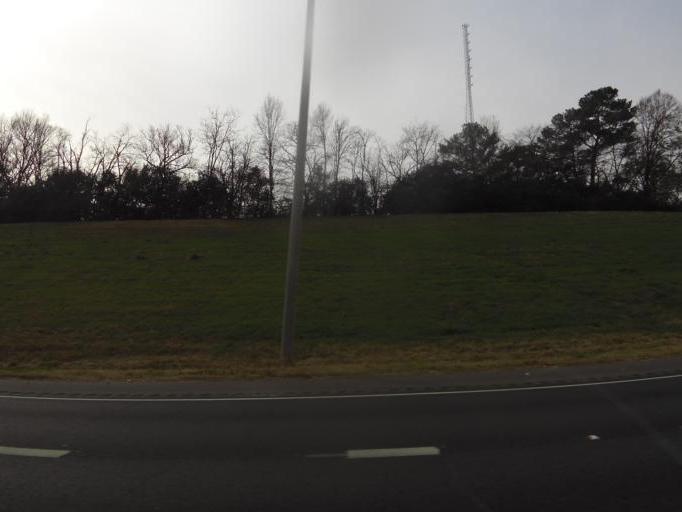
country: US
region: Alabama
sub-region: Montgomery County
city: Montgomery
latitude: 32.3675
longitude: -86.2932
